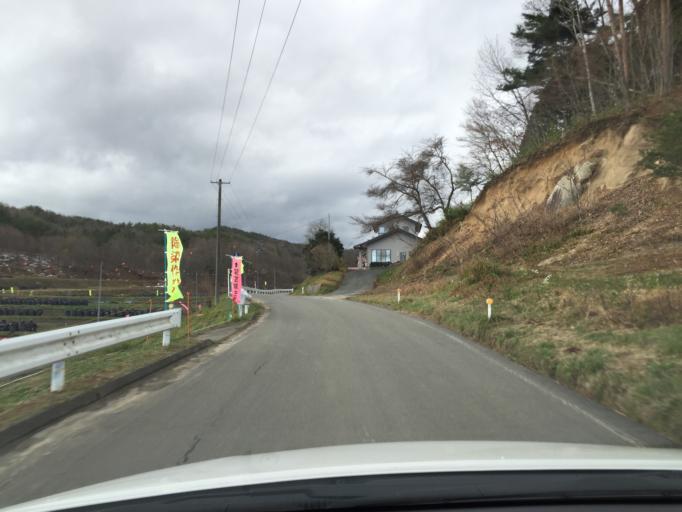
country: JP
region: Fukushima
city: Yanagawamachi-saiwaicho
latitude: 37.7131
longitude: 140.6885
